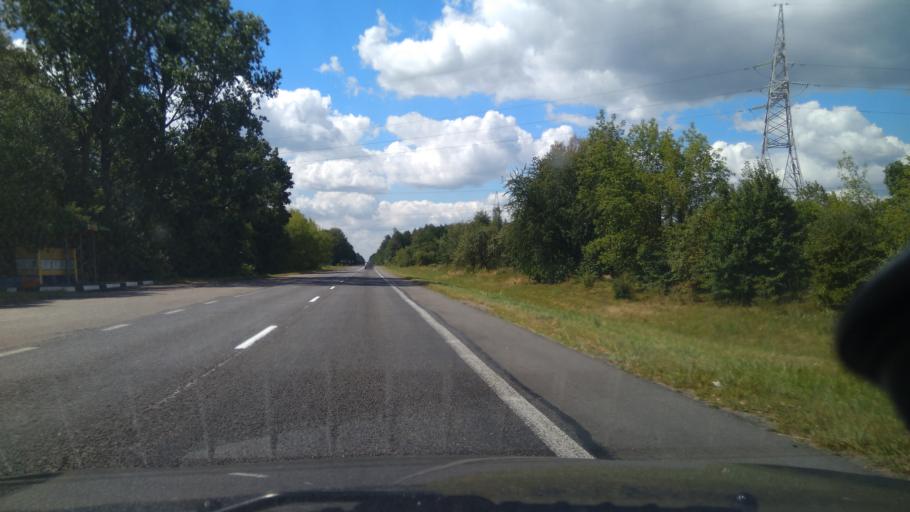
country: BY
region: Brest
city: Nyakhachava
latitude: 52.6758
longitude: 25.2700
